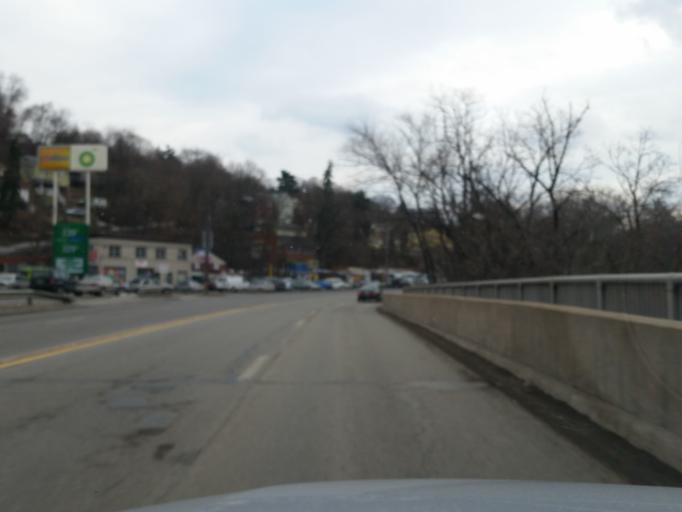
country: US
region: Pennsylvania
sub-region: Allegheny County
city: Mount Oliver
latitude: 40.3958
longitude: -79.9979
